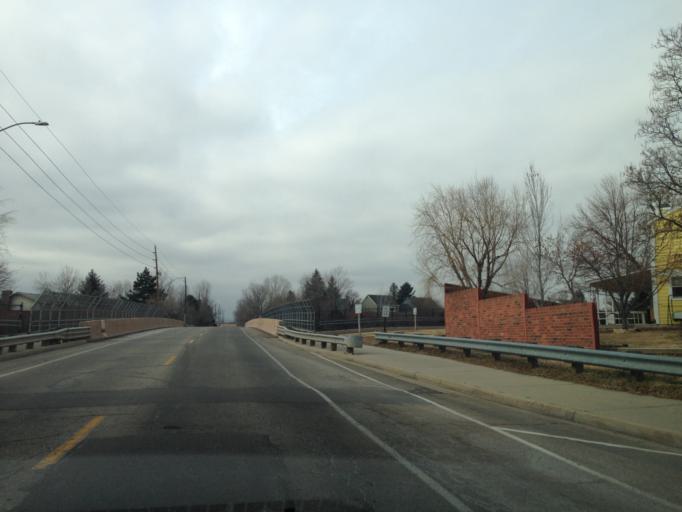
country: US
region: Colorado
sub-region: Boulder County
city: Lafayette
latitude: 39.9942
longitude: -105.1016
